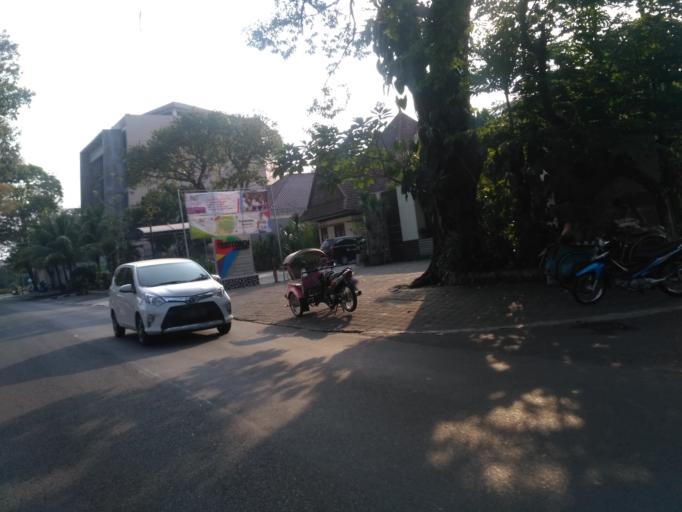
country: ID
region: East Java
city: Malang
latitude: -7.9683
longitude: 112.6250
